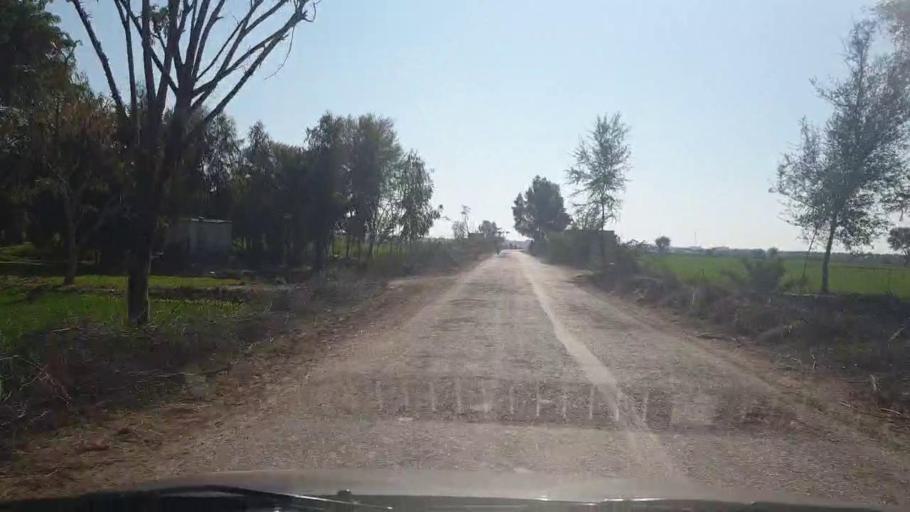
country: PK
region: Sindh
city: Bozdar
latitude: 27.1655
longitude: 68.6438
